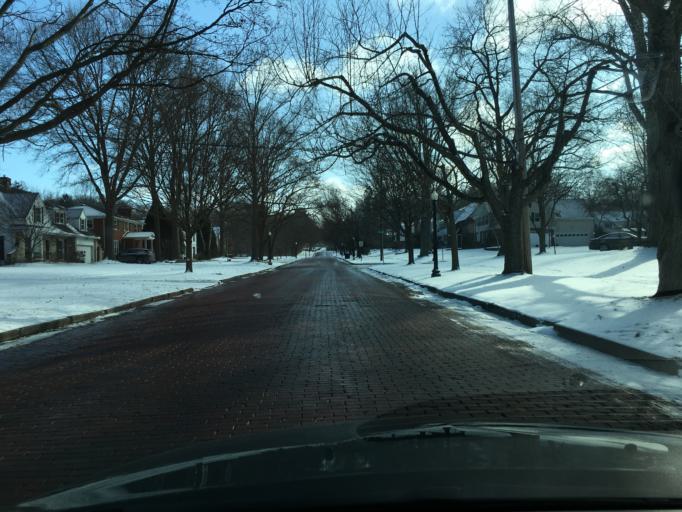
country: US
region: Ohio
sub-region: Summit County
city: Akron
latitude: 41.0994
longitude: -81.5613
